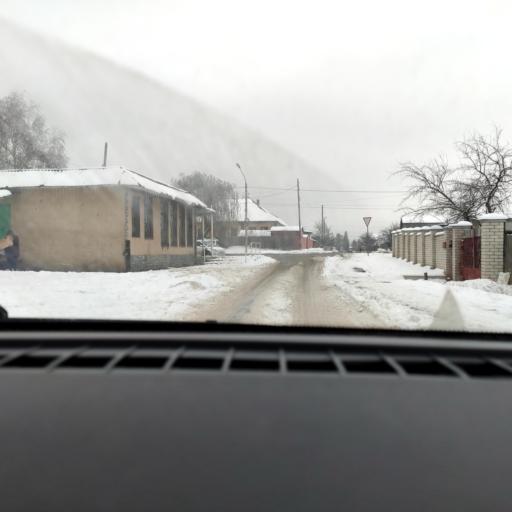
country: RU
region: Voronezj
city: Maslovka
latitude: 51.6108
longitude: 39.2207
